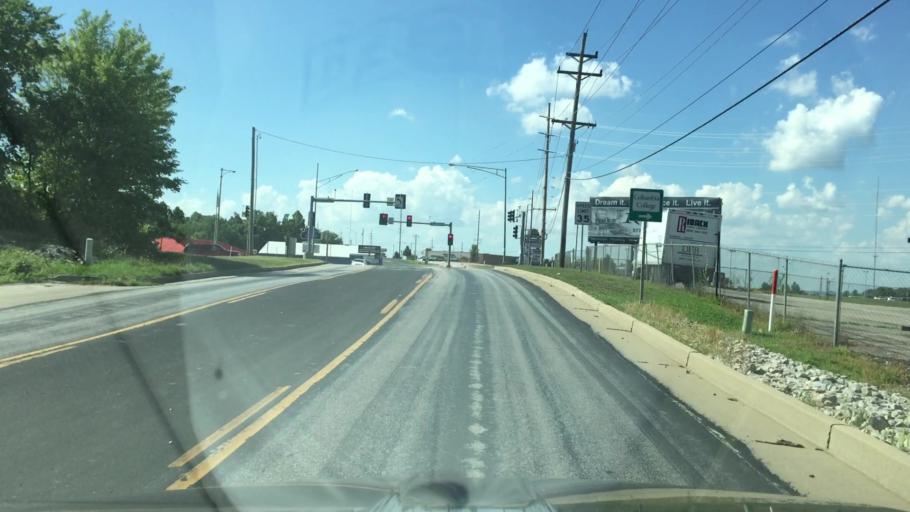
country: US
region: Missouri
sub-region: Camden County
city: Osage Beach
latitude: 38.1537
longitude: -92.6019
